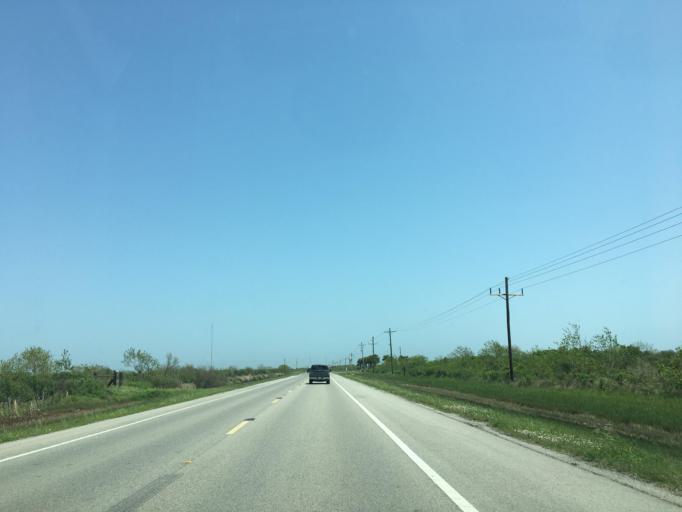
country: US
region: Texas
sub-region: Galveston County
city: Galveston
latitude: 29.4059
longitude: -94.7198
